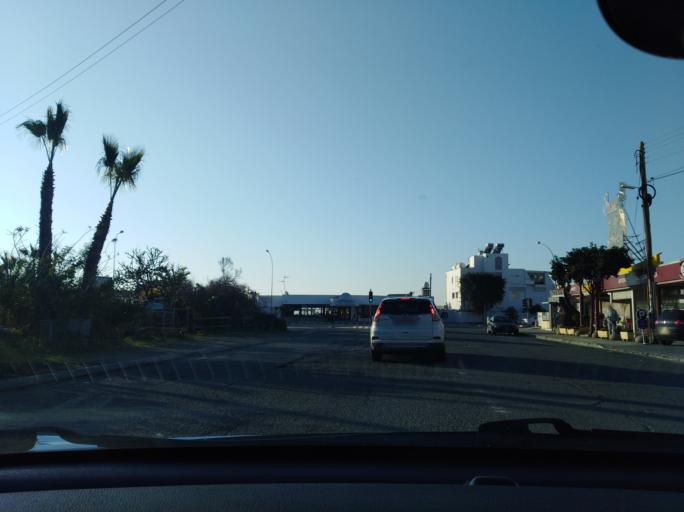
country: CY
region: Limassol
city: Mouttagiaka
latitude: 34.7030
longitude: 33.1066
